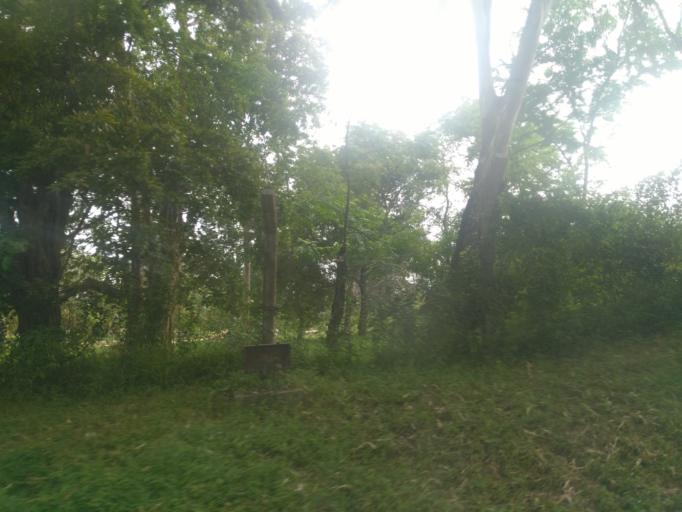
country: TZ
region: Zanzibar Urban/West
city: Zanzibar
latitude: -6.1730
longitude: 39.2037
